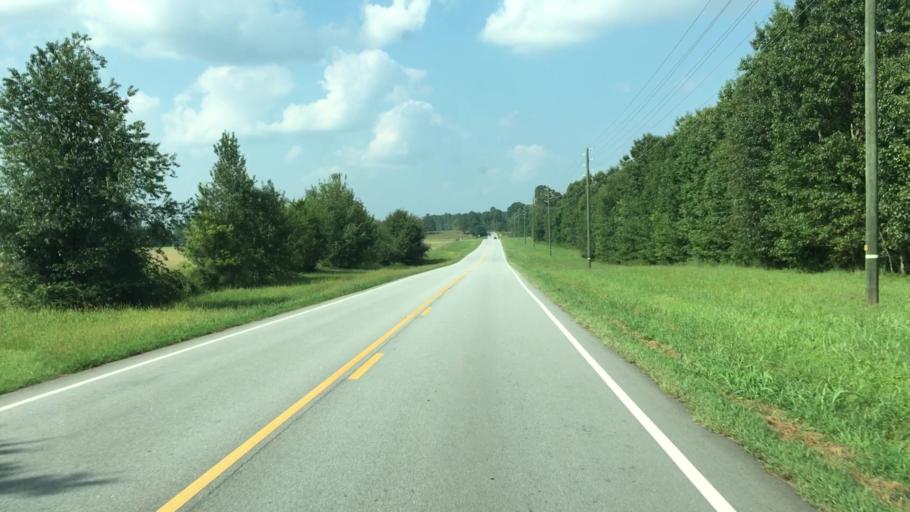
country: US
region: Georgia
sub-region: Jasper County
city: Monticello
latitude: 33.4477
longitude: -83.7557
